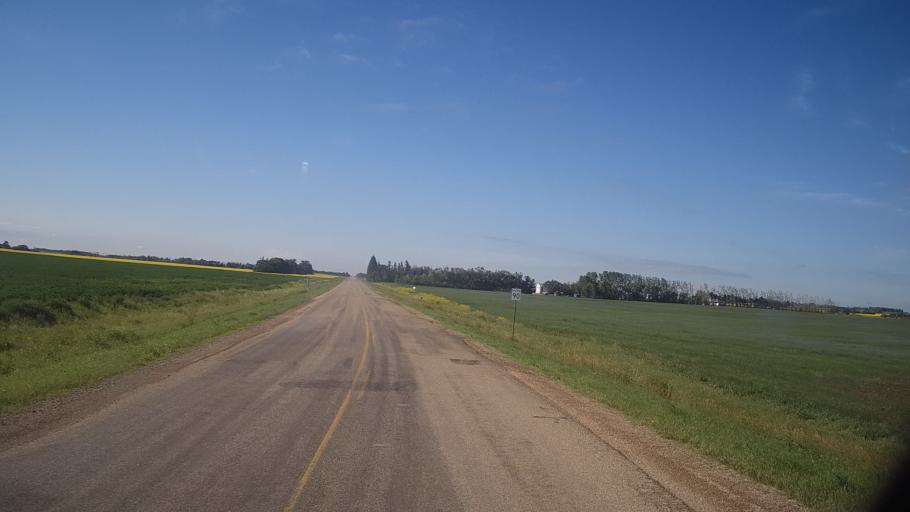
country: CA
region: Saskatchewan
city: Watrous
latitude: 51.8206
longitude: -105.2866
